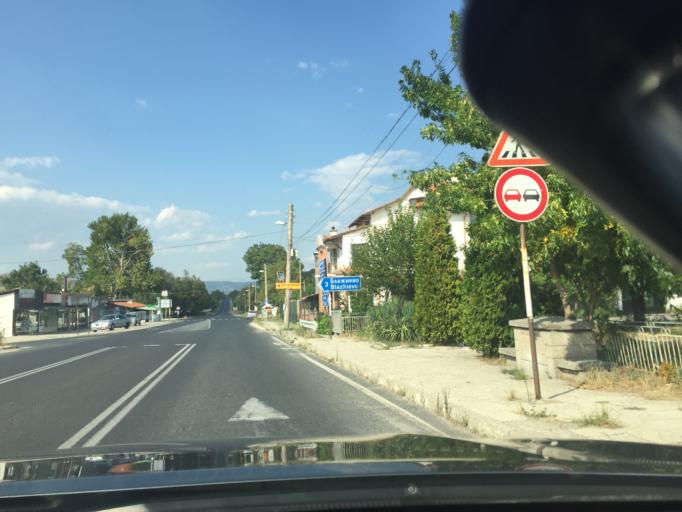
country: BG
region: Kyustendil
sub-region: Obshtina Boboshevo
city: Boboshevo
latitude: 42.1921
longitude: 23.0598
